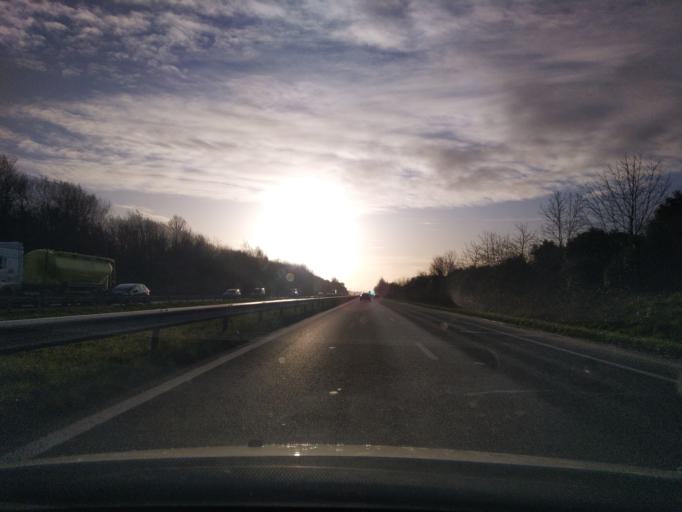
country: FR
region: Haute-Normandie
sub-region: Departement de la Seine-Maritime
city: Maromme
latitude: 49.4779
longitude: 1.0170
